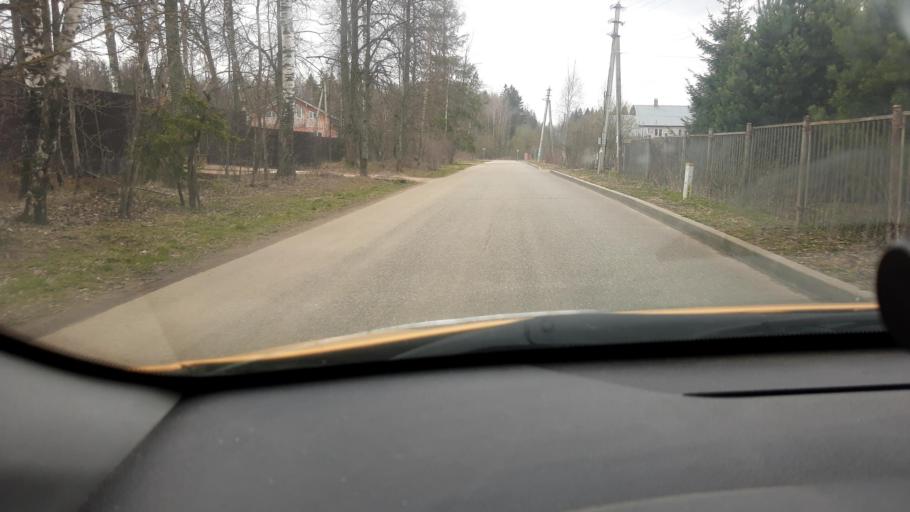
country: RU
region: Moskovskaya
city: Povarovo
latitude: 56.0218
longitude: 36.9907
